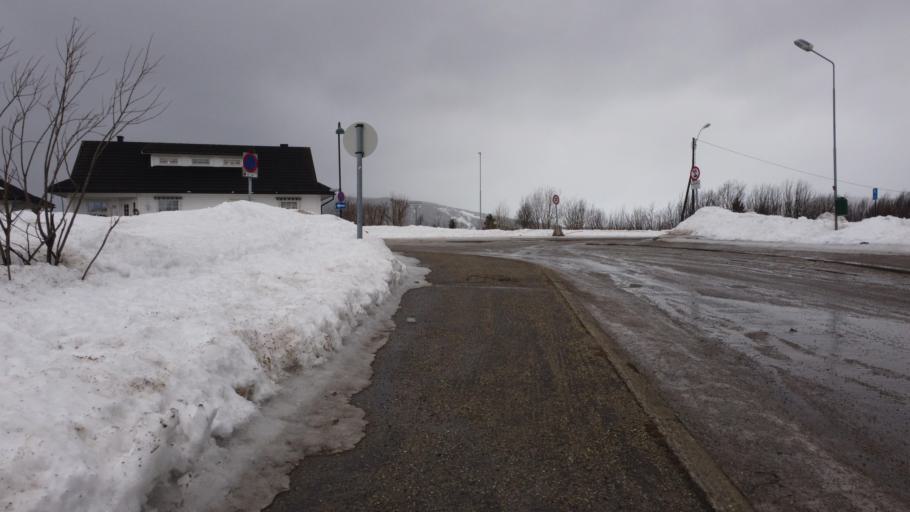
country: NO
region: Nordland
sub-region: Rana
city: Mo i Rana
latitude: 66.3182
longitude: 14.1582
